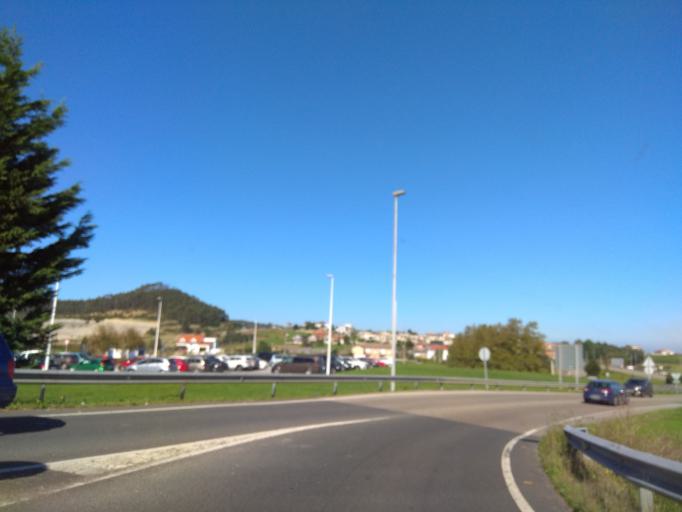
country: ES
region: Cantabria
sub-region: Provincia de Cantabria
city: Santa Cruz de Bezana
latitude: 43.4326
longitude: -3.9186
